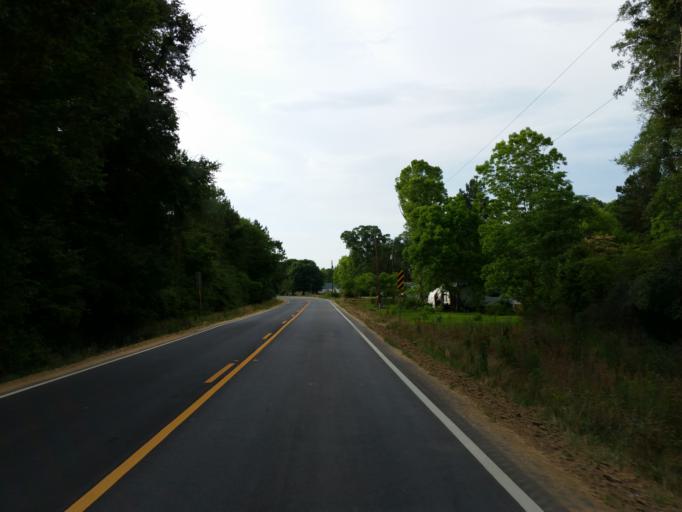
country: US
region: Georgia
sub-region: Turner County
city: Ashburn
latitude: 31.7646
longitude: -83.6854
